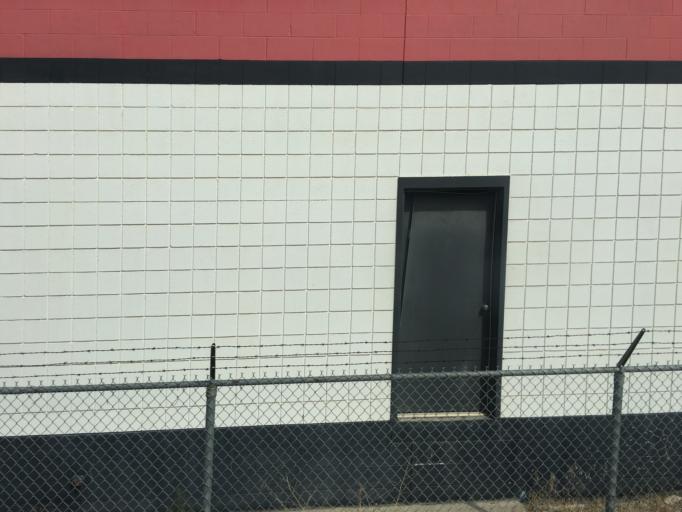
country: US
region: Utah
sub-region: Salt Lake County
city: Salt Lake City
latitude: 40.7669
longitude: -111.9111
